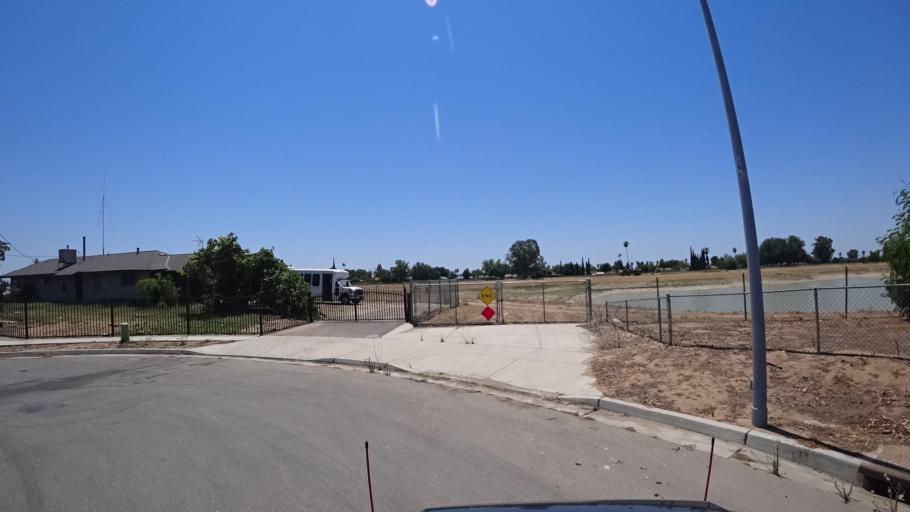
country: US
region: California
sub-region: Fresno County
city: West Park
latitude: 36.7334
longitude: -119.8317
